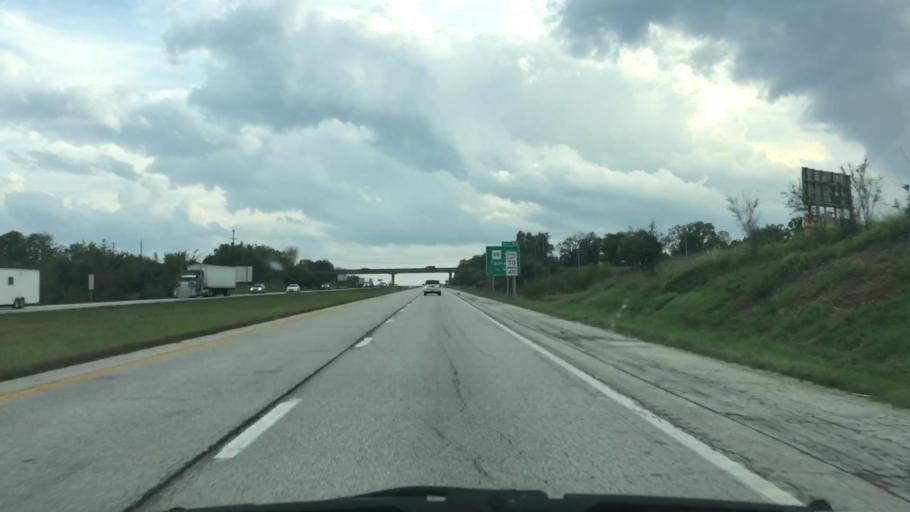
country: US
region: Missouri
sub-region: Clinton County
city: Cameron
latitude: 39.7453
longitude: -94.2203
